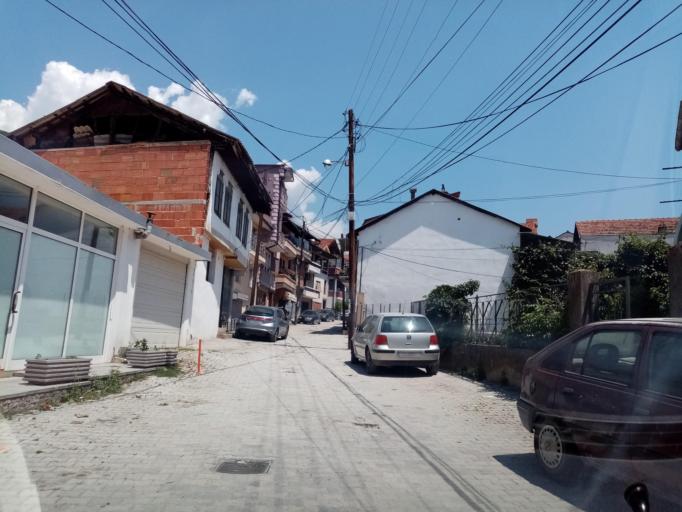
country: MK
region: Tetovo
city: Tetovo
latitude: 42.0153
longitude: 20.9701
